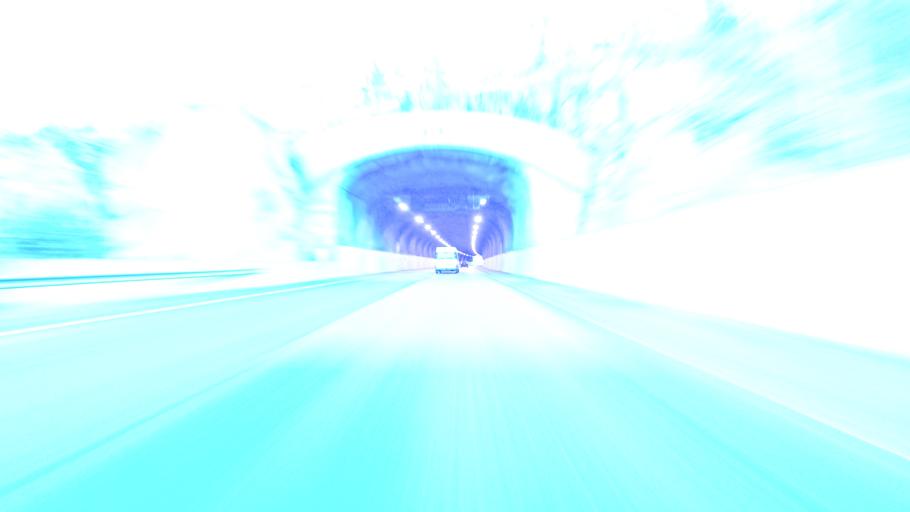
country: FI
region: Uusimaa
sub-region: Helsinki
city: Lohja
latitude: 60.3033
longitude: 24.0481
